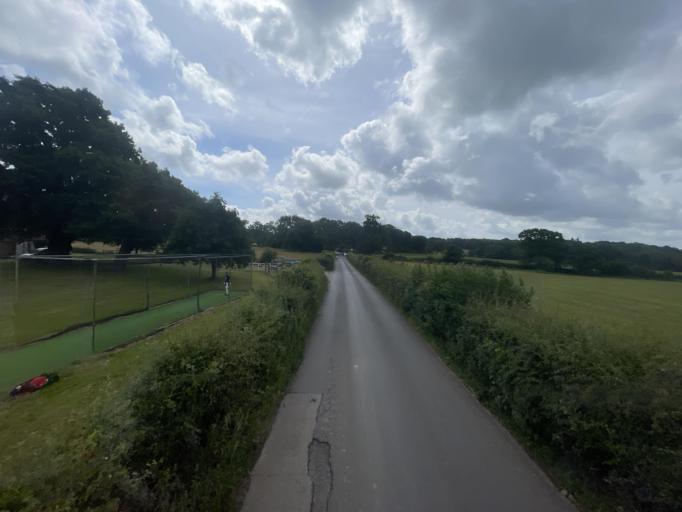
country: GB
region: England
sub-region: Kent
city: Edenbridge
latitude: 51.1585
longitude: 0.1488
